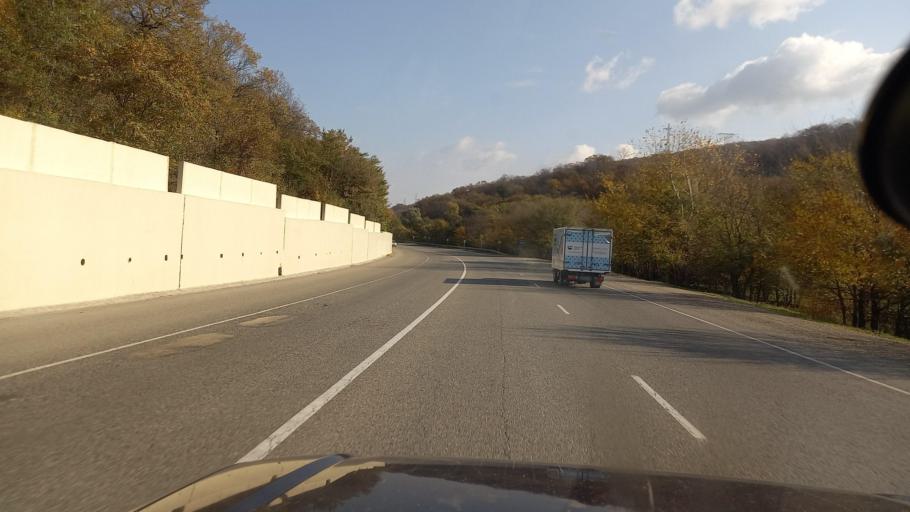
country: RU
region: Krasnodarskiy
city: Verkhnebakanskiy
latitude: 44.8435
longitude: 37.7158
